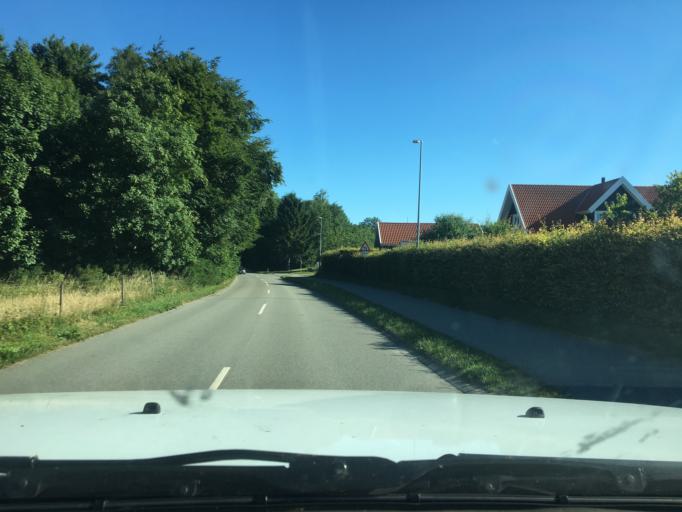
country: DK
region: Central Jutland
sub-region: Syddjurs Kommune
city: Hornslet
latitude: 56.3157
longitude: 10.3032
